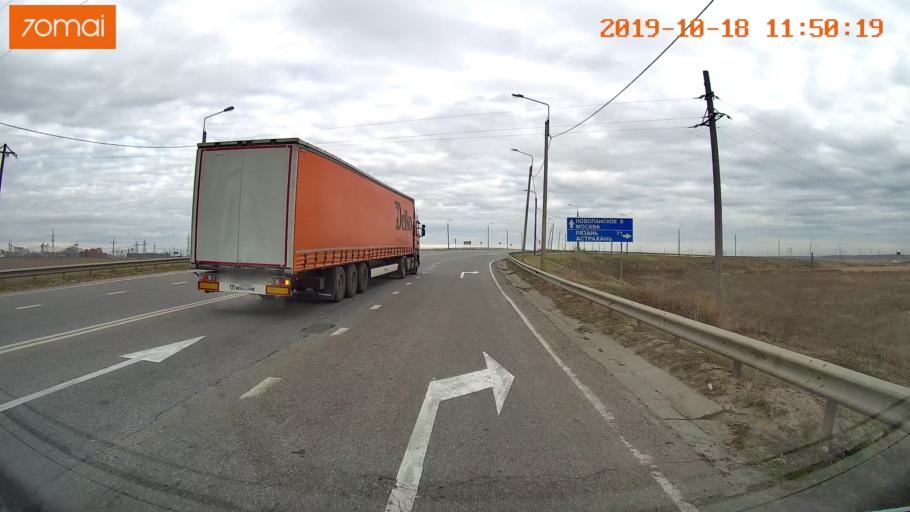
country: RU
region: Rjazan
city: Mikhaylov
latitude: 54.2599
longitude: 39.0024
